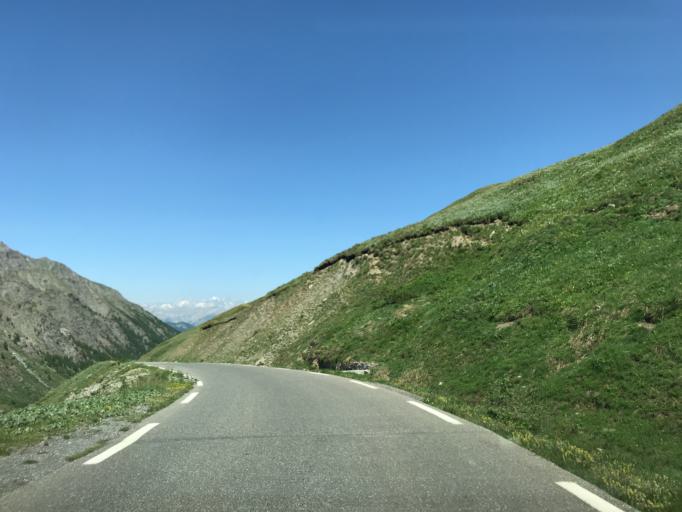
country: IT
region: Piedmont
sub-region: Provincia di Cuneo
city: Pontechianale
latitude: 44.6961
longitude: 6.9557
